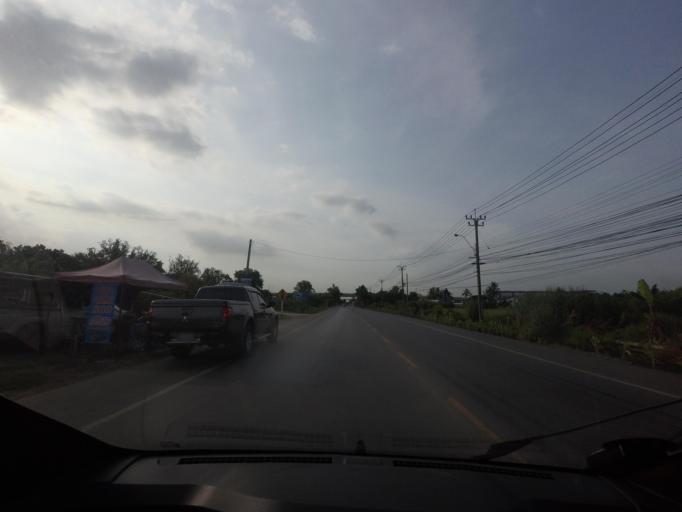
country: TH
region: Bangkok
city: Nong Chok
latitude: 13.8011
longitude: 100.8722
